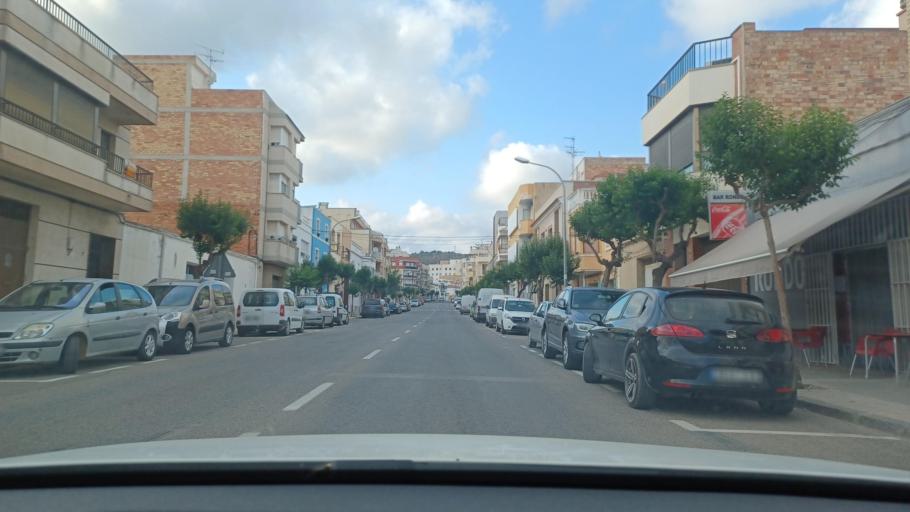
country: ES
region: Catalonia
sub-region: Provincia de Tarragona
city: Alcanar
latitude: 40.5415
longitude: 0.4775
